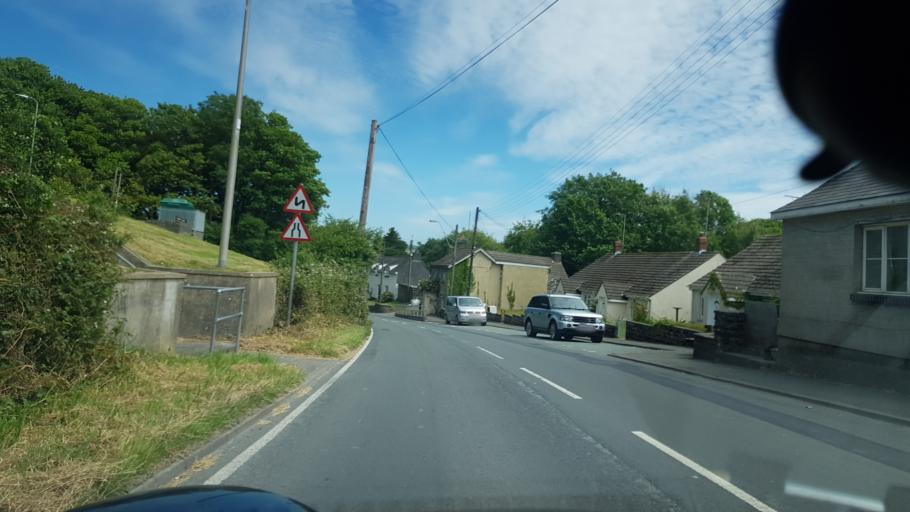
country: GB
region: Wales
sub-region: Carmarthenshire
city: Saint Clears
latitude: 51.7661
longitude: -4.4645
